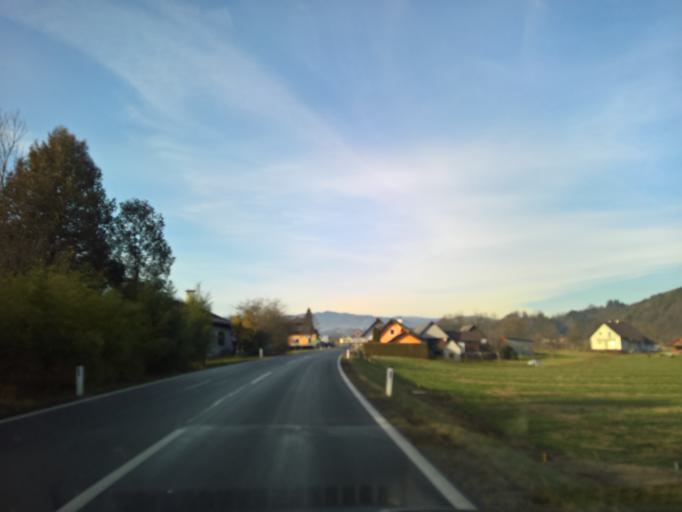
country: AT
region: Styria
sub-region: Politischer Bezirk Leibnitz
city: Oberhaag
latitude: 46.6929
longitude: 15.3205
